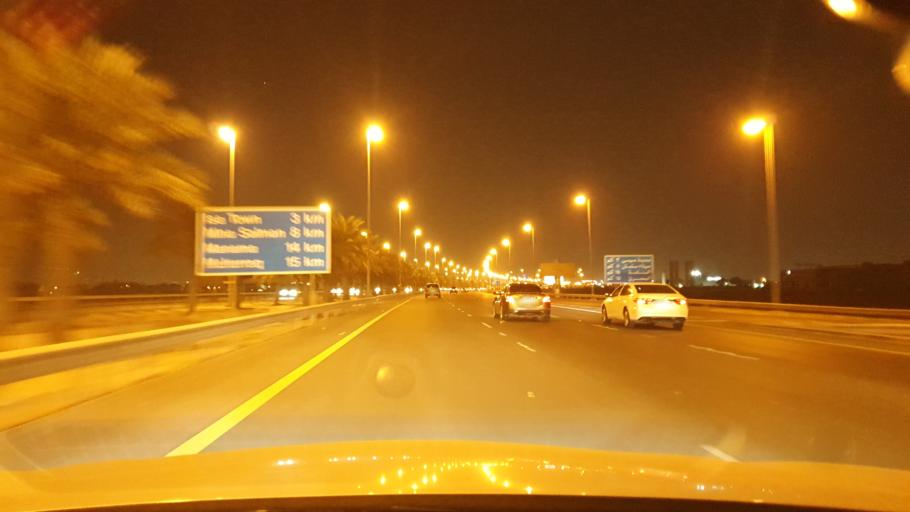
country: BH
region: Northern
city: Madinat `Isa
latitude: 26.1941
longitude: 50.5196
